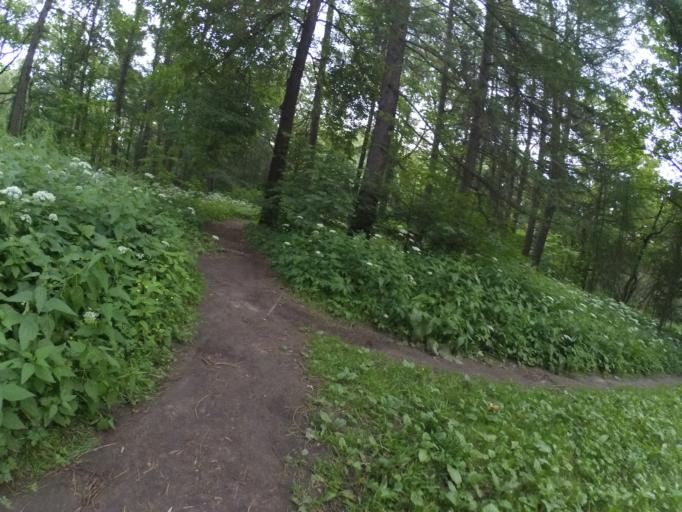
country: RU
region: Moscow
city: Novovladykino
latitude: 55.8439
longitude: 37.5996
